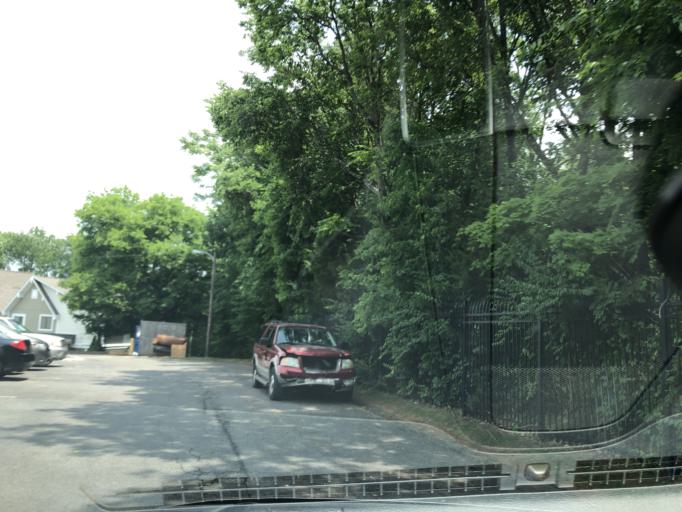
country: US
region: Tennessee
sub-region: Davidson County
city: Oak Hill
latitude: 36.0654
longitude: -86.6909
